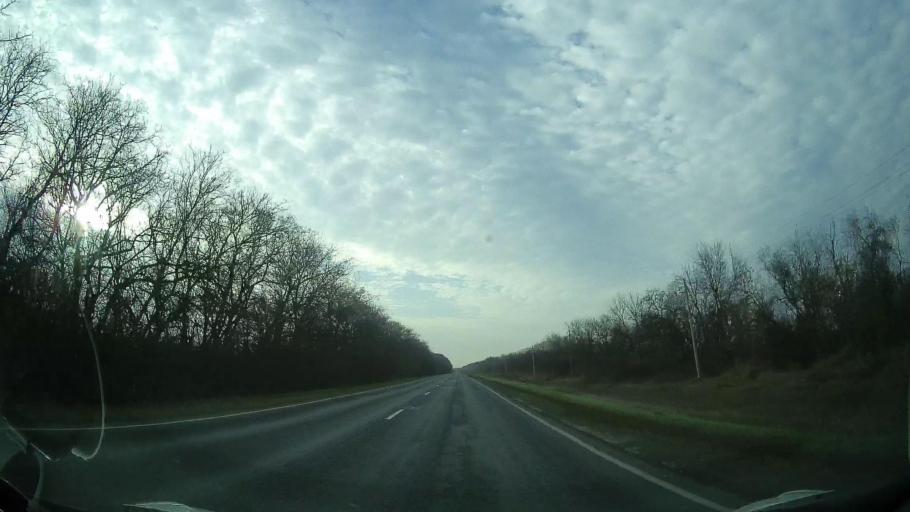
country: RU
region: Rostov
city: Bagayevskaya
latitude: 47.0928
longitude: 40.3664
